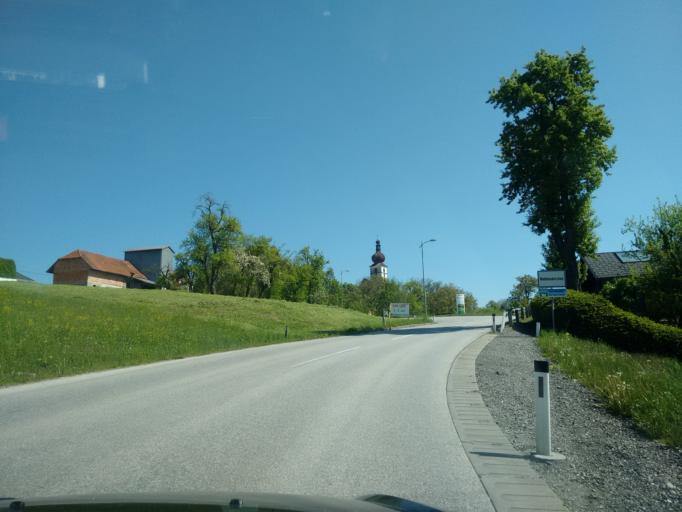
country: AT
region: Upper Austria
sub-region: Politischer Bezirk Steyr-Land
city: Waldneukirchen
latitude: 47.9941
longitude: 14.2584
